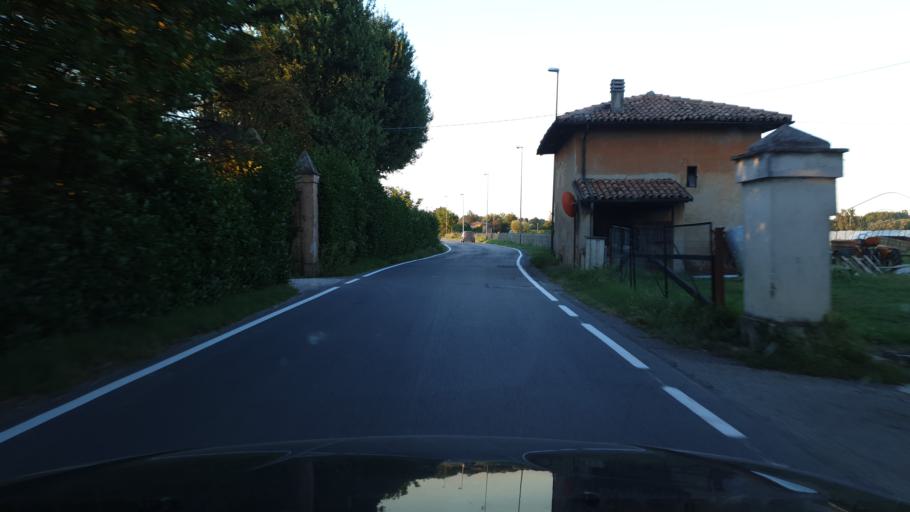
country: IT
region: Emilia-Romagna
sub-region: Provincia di Bologna
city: Quarto Inferiore
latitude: 44.5197
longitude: 11.3900
